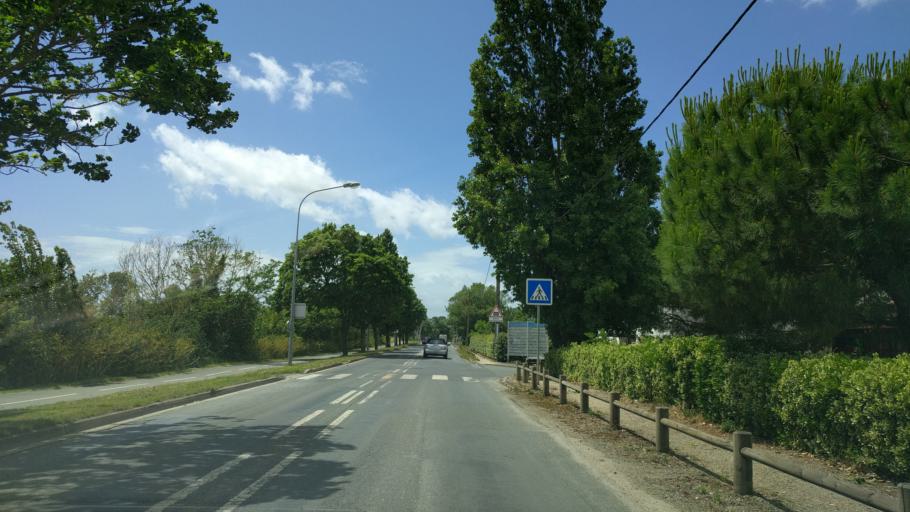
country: FR
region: Poitou-Charentes
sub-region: Departement de la Charente-Maritime
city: La Rochelle
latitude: 46.1578
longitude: -1.1377
